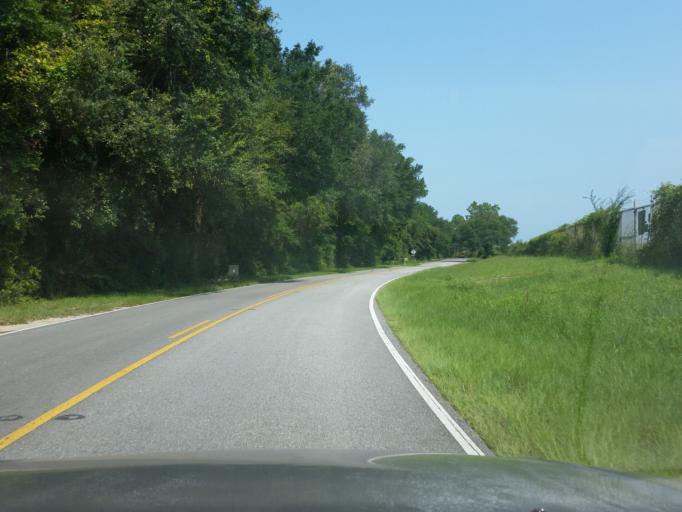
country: US
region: Florida
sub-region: Escambia County
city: Bellview
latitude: 30.4648
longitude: -87.3488
